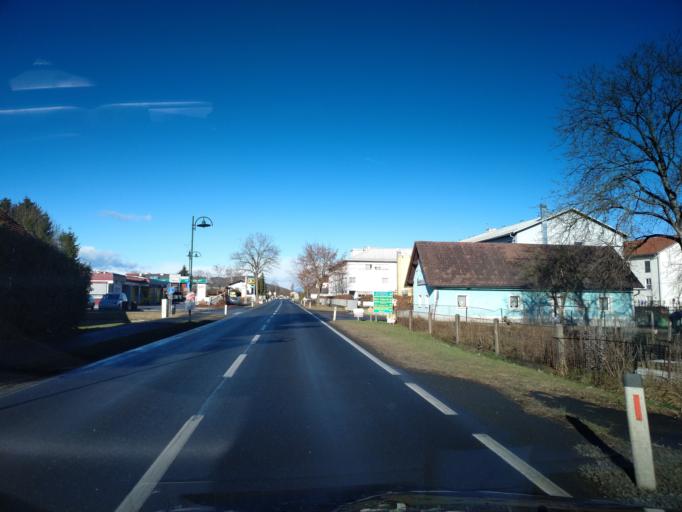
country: AT
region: Styria
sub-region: Politischer Bezirk Leibnitz
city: Kaindorf an der Sulm
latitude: 46.8155
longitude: 15.5481
